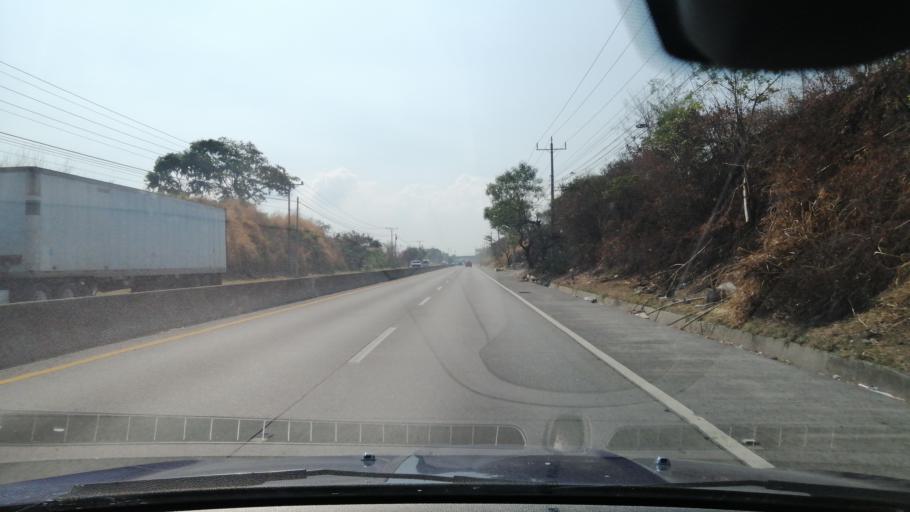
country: SV
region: San Salvador
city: Apopa
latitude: 13.7913
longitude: -89.2225
